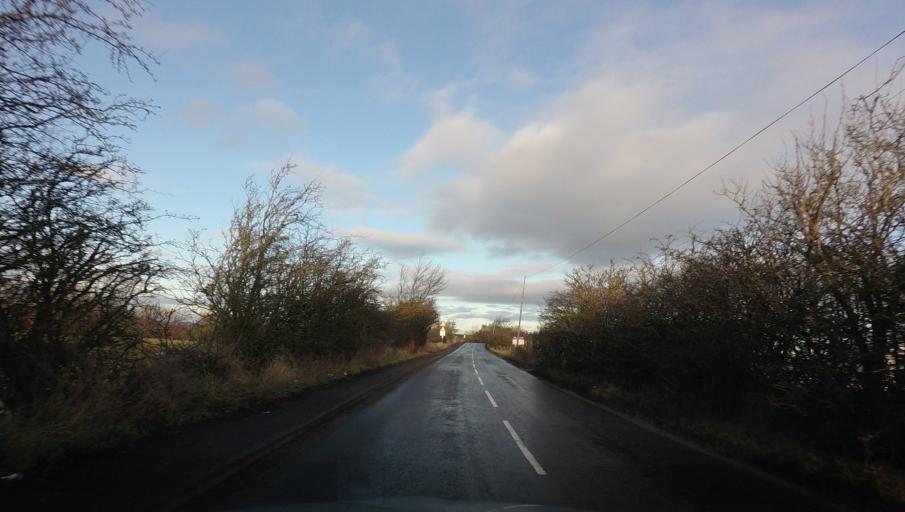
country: GB
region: Scotland
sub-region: West Lothian
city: East Calder
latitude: 55.8950
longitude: -3.4426
